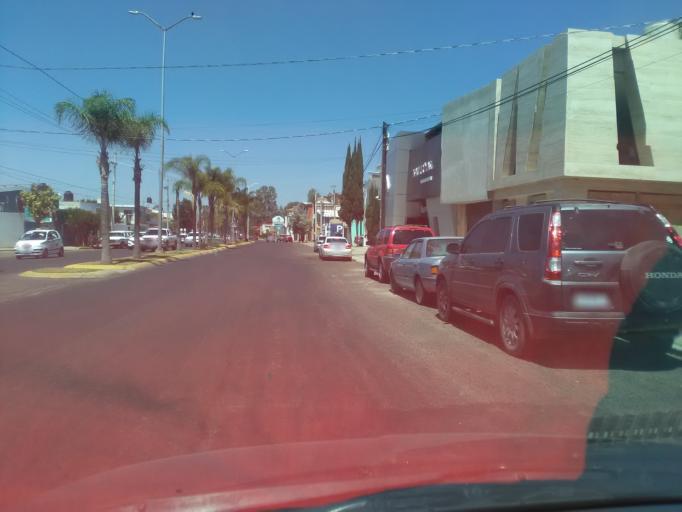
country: MX
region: Durango
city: Victoria de Durango
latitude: 24.0138
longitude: -104.6799
